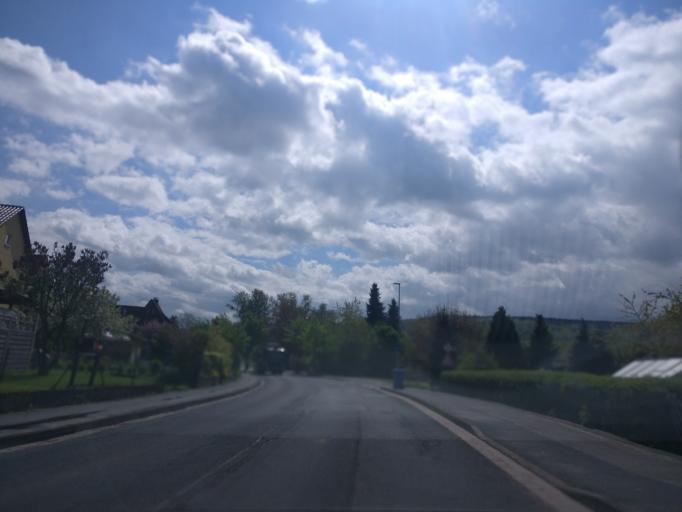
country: DE
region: Lower Saxony
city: Hannoversch Munden
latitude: 51.4358
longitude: 9.6406
